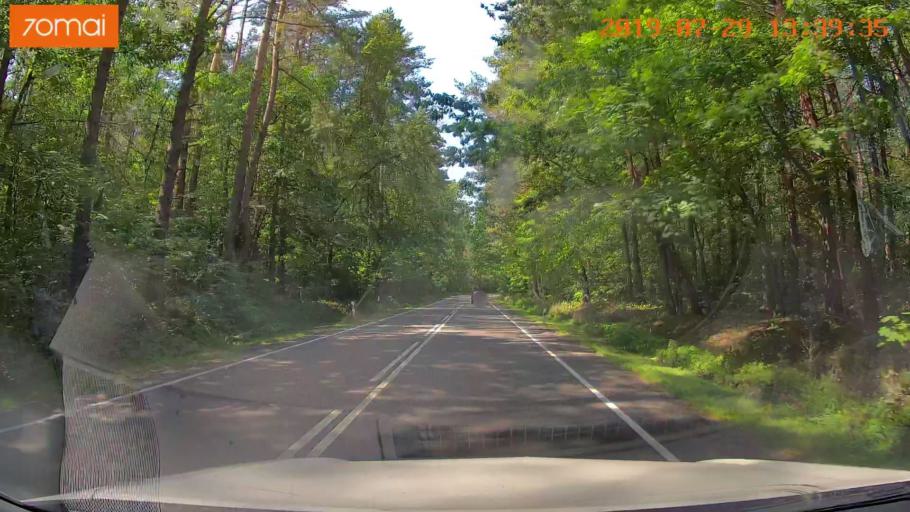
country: RU
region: Kaliningrad
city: Svetlyy
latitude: 54.7243
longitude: 20.1508
